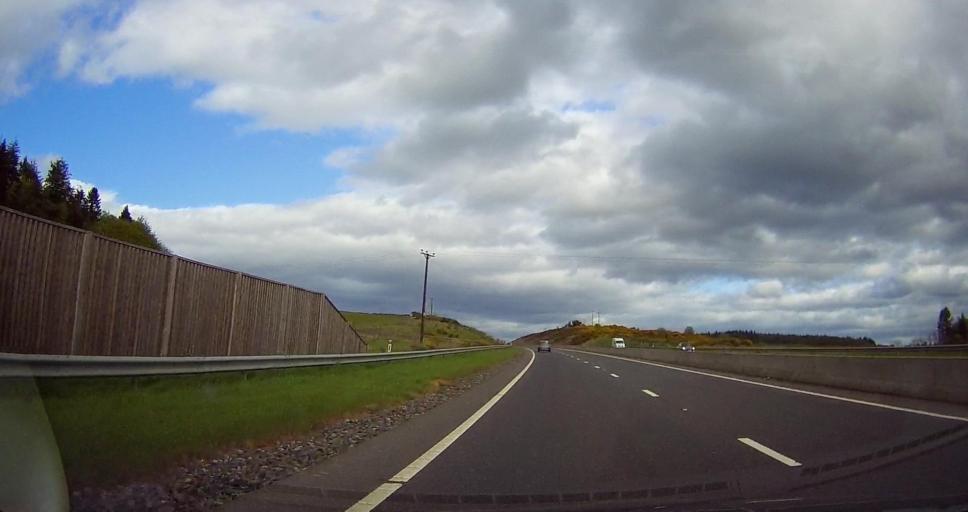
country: GB
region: Scotland
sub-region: Aberdeen City
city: Cults
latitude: 57.0778
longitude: -2.1994
